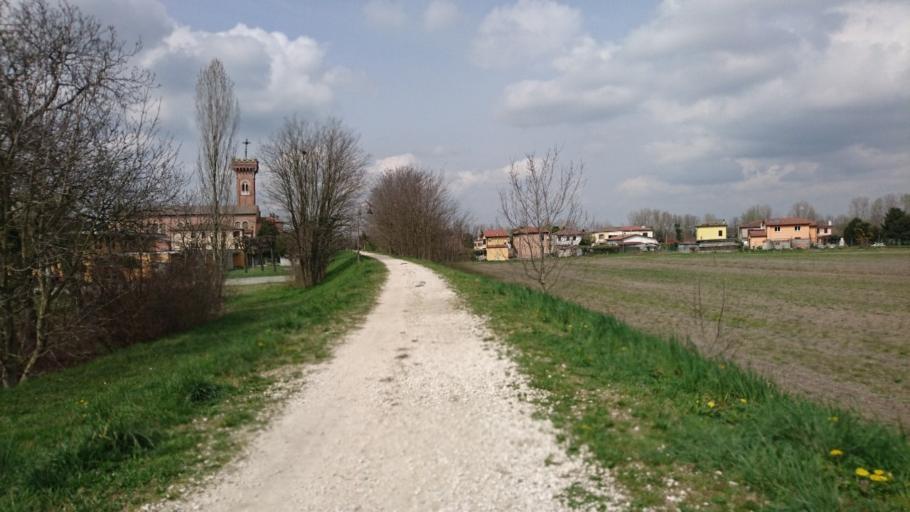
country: IT
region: Veneto
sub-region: Provincia di Padova
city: Limena
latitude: 45.4750
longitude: 11.8493
